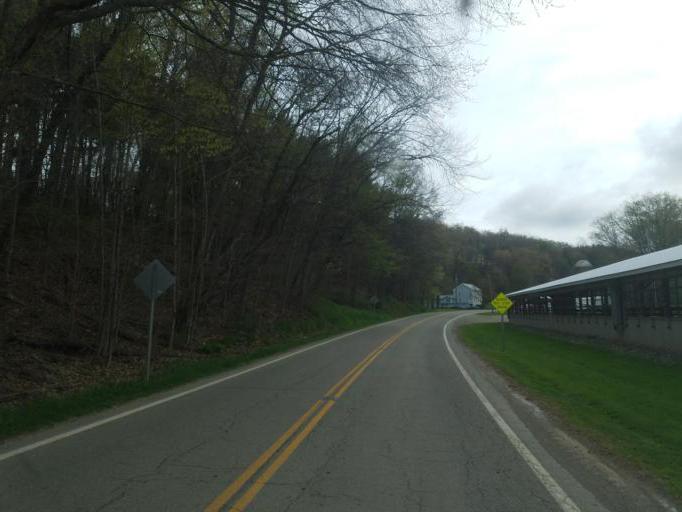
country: US
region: Ohio
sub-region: Ashland County
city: Loudonville
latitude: 40.5395
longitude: -82.1792
